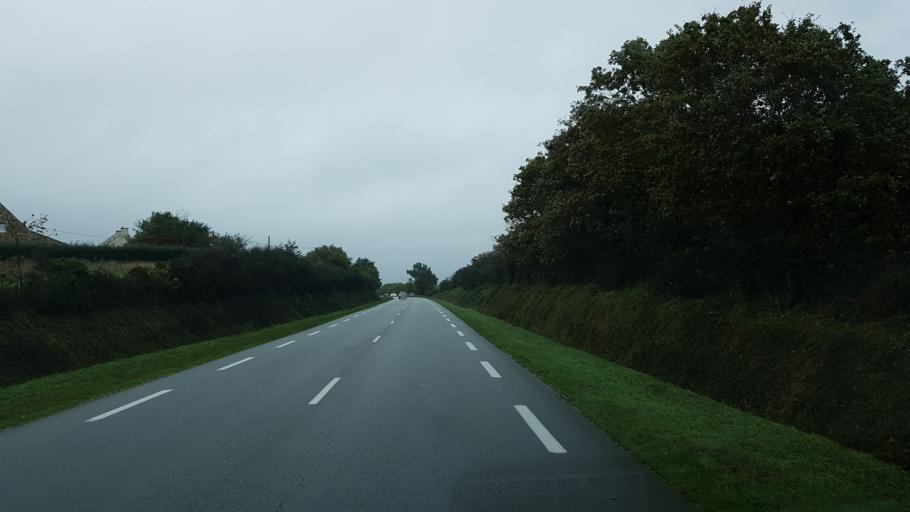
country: FR
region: Brittany
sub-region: Departement du Morbihan
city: Theix
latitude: 47.5910
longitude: -2.6848
